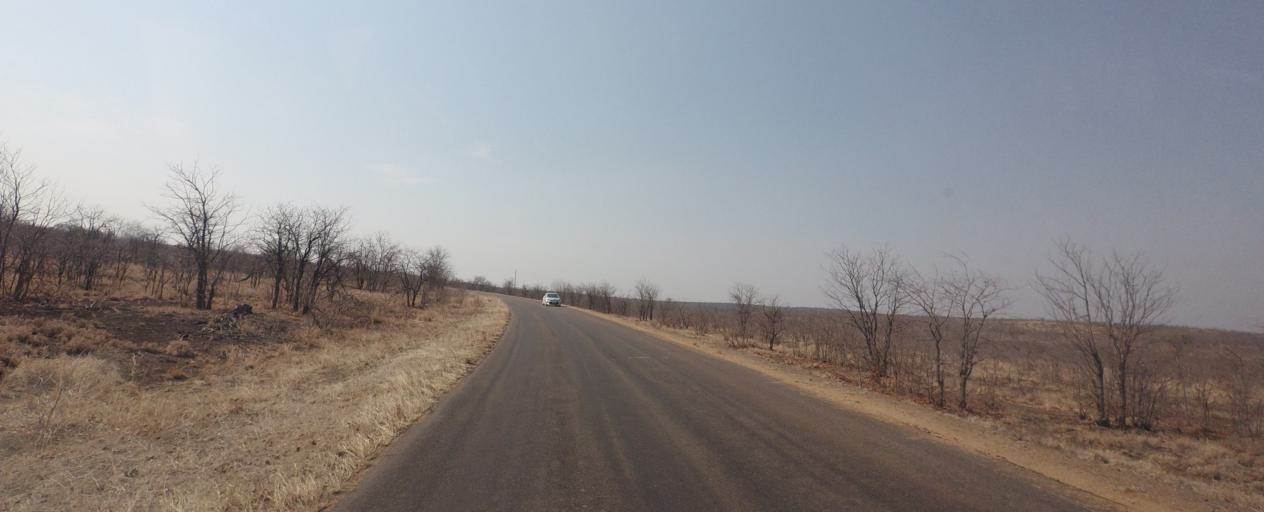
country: ZA
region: Limpopo
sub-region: Mopani District Municipality
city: Phalaborwa
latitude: -23.9823
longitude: 31.6431
